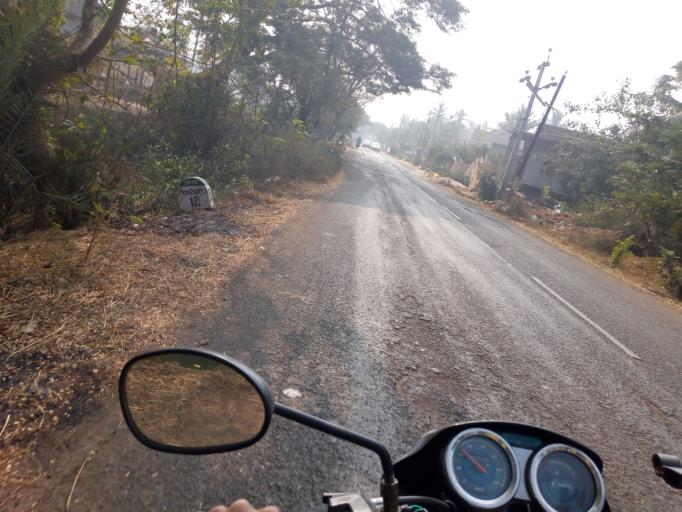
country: IN
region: Andhra Pradesh
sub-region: West Godavari
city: Tadepallegudem
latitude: 16.7810
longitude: 81.4201
